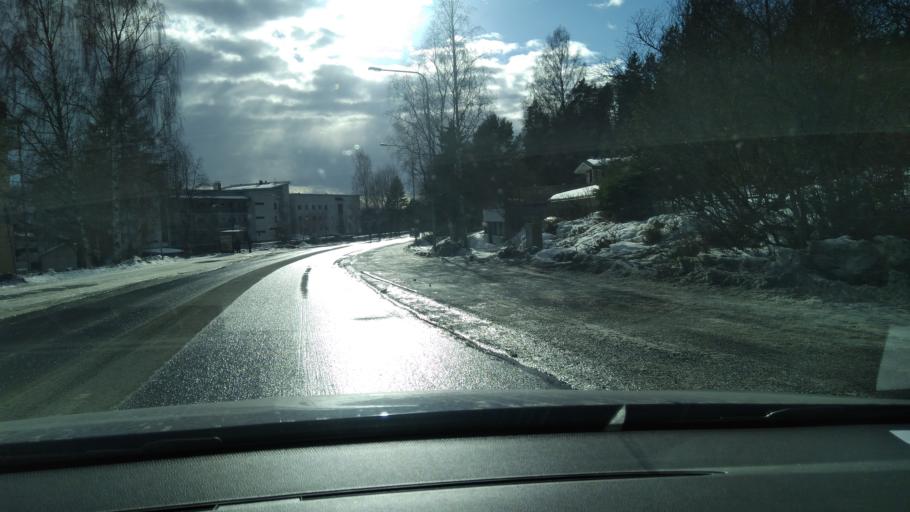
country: FI
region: Pirkanmaa
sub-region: Tampere
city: Pirkkala
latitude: 61.4986
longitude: 23.6355
